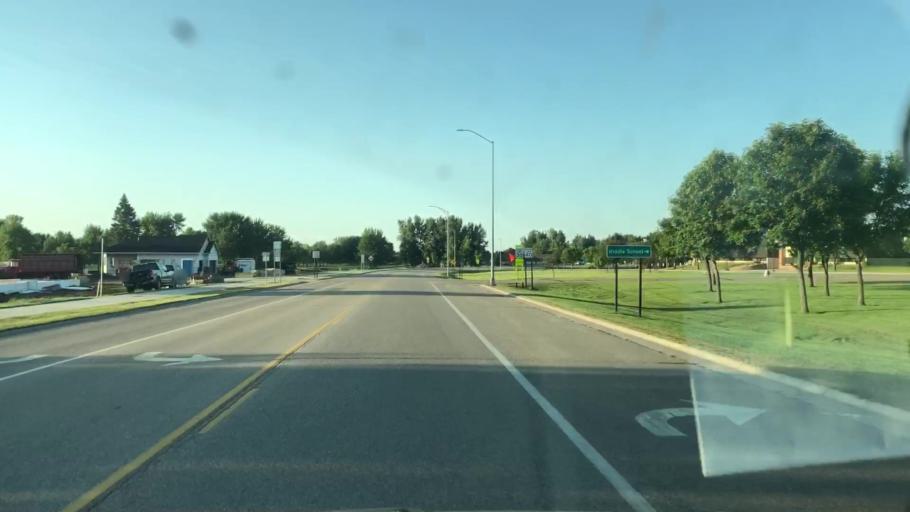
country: US
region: Minnesota
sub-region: Nobles County
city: Worthington
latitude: 43.6306
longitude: -95.6287
